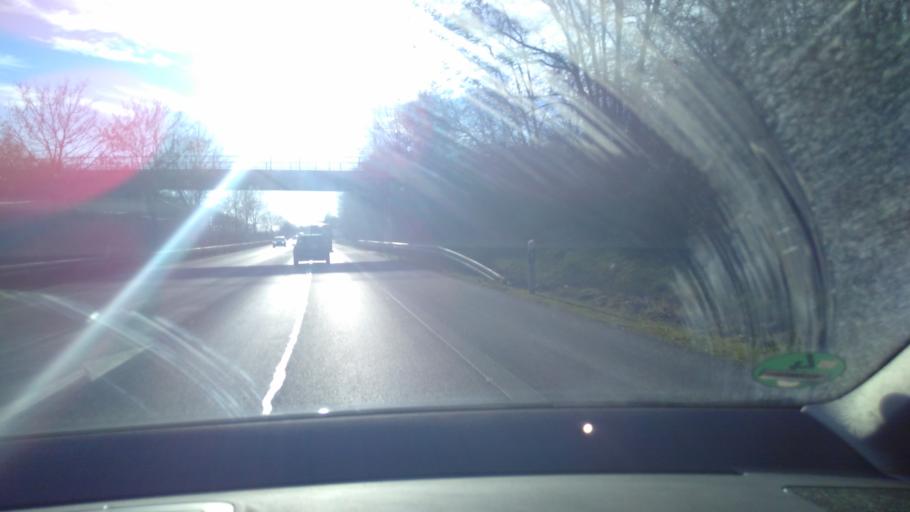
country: DE
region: North Rhine-Westphalia
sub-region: Regierungsbezirk Koln
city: Bergheim
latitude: 50.9560
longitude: 6.6130
